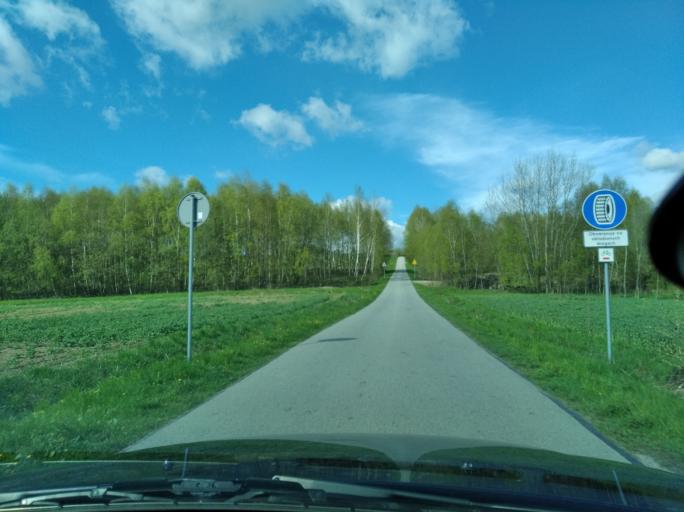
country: PL
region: Subcarpathian Voivodeship
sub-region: Powiat ropczycko-sedziszowski
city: Wielopole Skrzynskie
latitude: 49.9157
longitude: 21.6438
